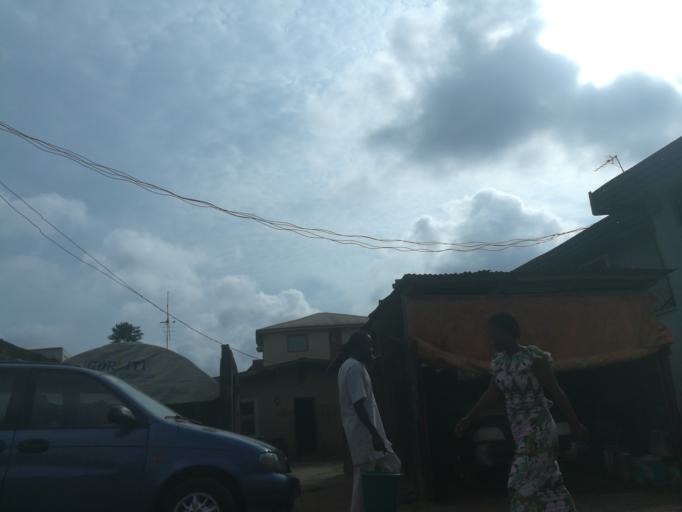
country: NG
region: Lagos
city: Agege
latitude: 6.6150
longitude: 3.3210
